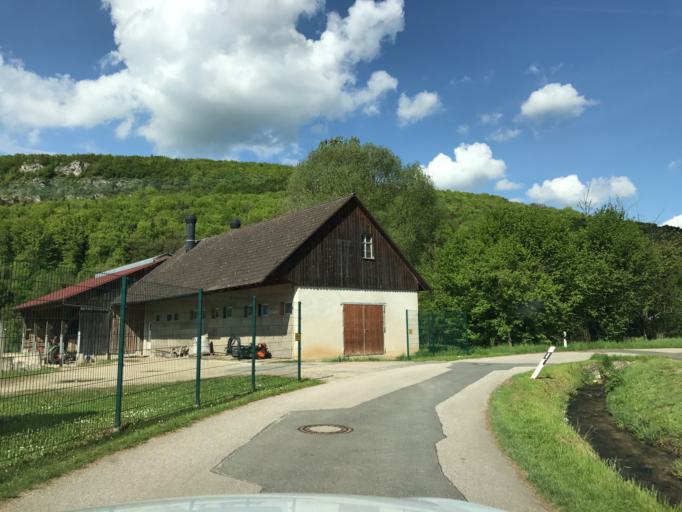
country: DE
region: Bavaria
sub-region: Upper Franconia
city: Egloffstein
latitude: 49.7316
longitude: 11.2314
